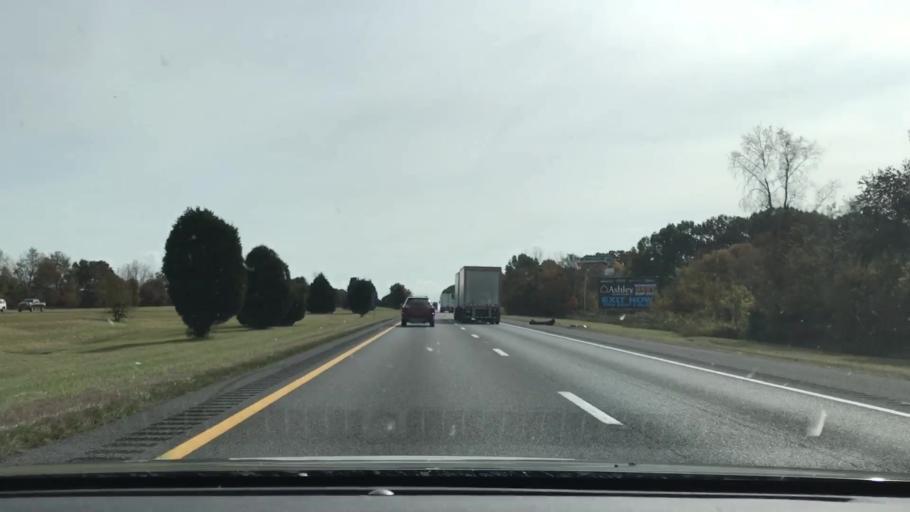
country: US
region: Tennessee
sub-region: Montgomery County
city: Clarksville
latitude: 36.6120
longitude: -87.2937
